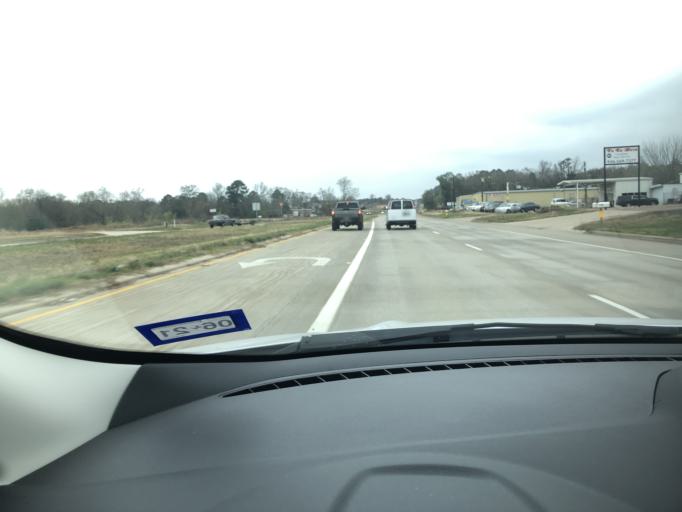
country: US
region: Texas
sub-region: Nacogdoches County
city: Nacogdoches
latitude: 31.5621
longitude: -94.6802
